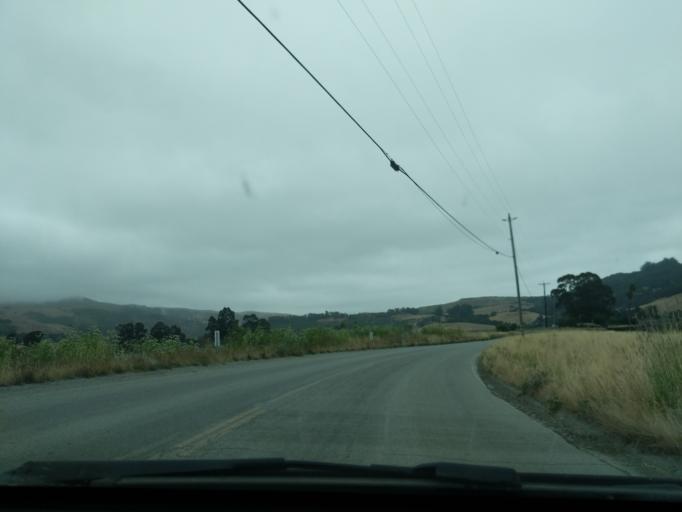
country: US
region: California
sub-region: San Benito County
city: Aromas
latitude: 36.8910
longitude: -121.6503
